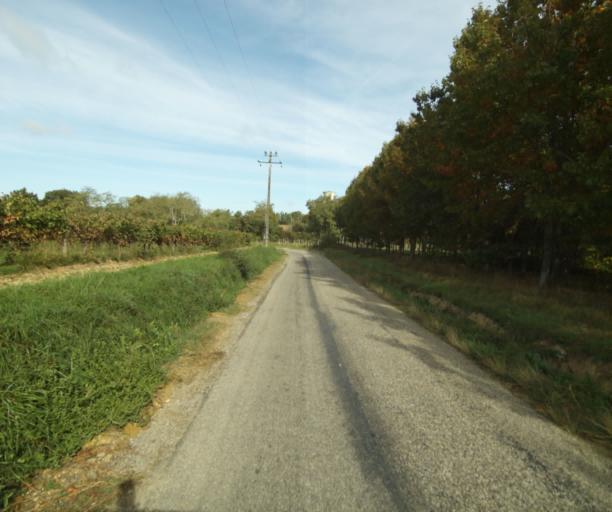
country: FR
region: Midi-Pyrenees
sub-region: Departement du Gers
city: Eauze
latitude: 43.8707
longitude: 0.1257
